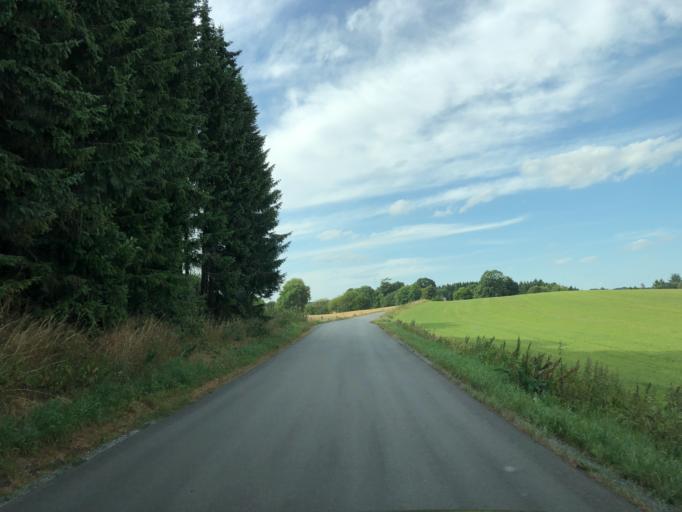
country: DK
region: South Denmark
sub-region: Vejle Kommune
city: Egtved
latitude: 55.6765
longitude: 9.2699
